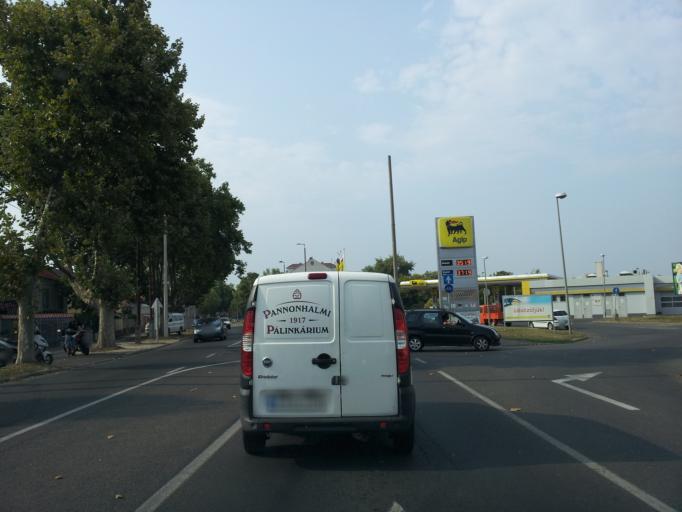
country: HU
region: Gyor-Moson-Sopron
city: Gyor
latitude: 47.6658
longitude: 17.6490
